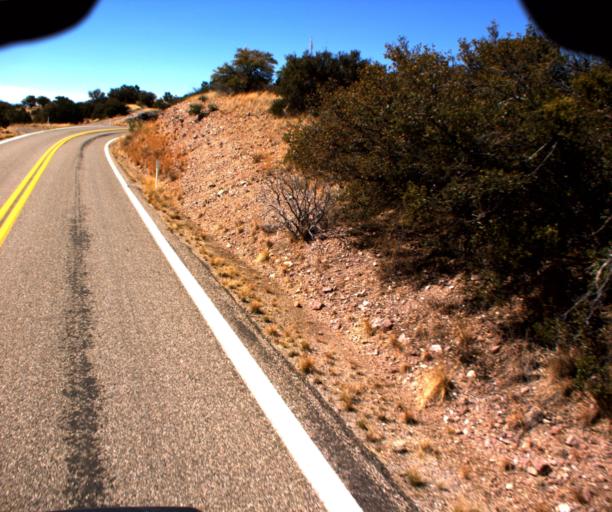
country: US
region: Arizona
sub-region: Cochise County
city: Sierra Vista
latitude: 31.4792
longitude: -110.4811
